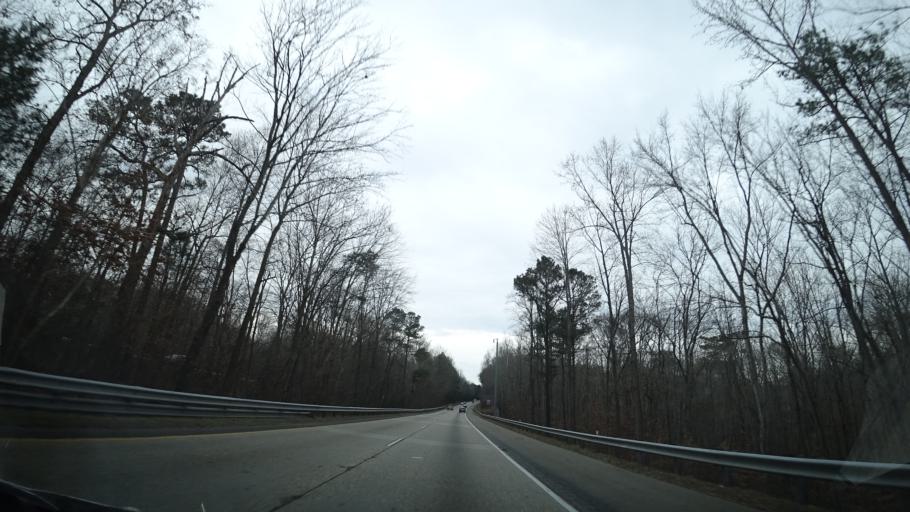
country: US
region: Virginia
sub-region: City of Williamsburg
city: Williamsburg
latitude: 37.2808
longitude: -76.6657
